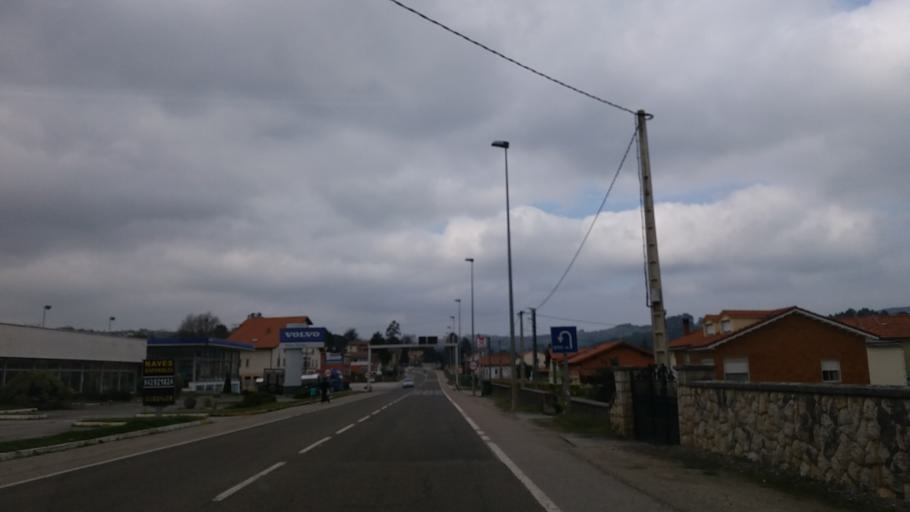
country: ES
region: Cantabria
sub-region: Provincia de Cantabria
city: Reocin
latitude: 43.3554
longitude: -4.1104
